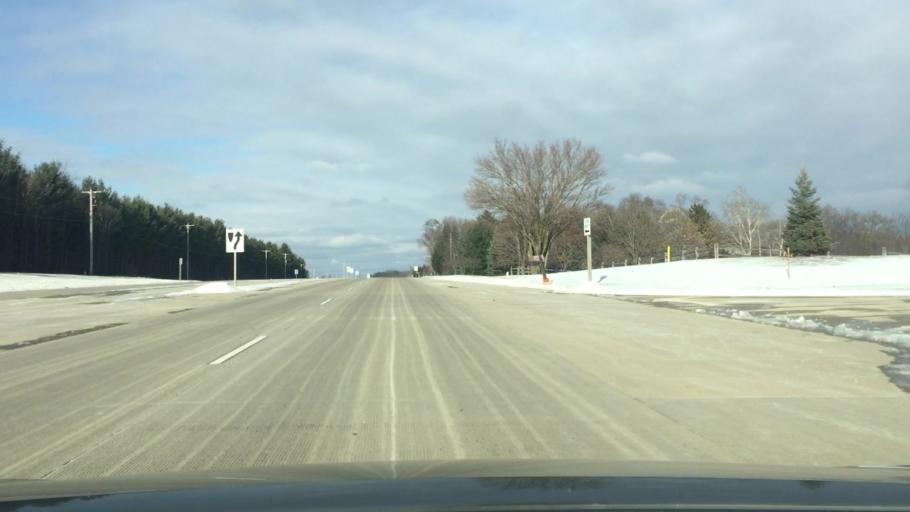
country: US
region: Wisconsin
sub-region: Waukesha County
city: Mukwonago
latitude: 42.8861
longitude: -88.3434
